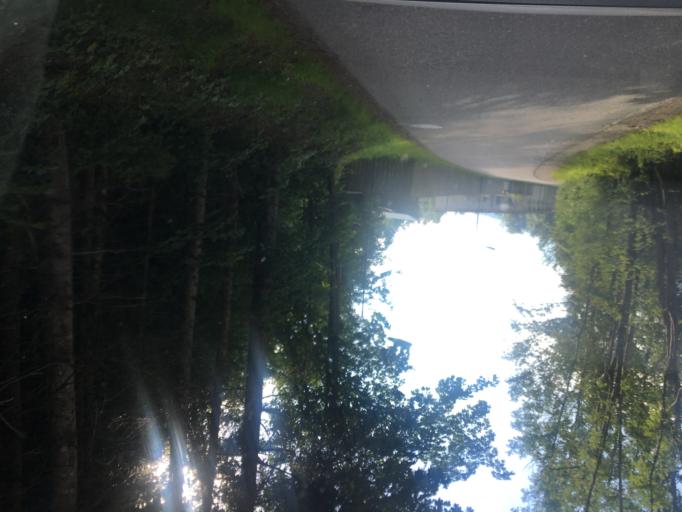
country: AT
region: Styria
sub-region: Politischer Bezirk Liezen
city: Schladming
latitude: 47.3966
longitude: 13.7002
